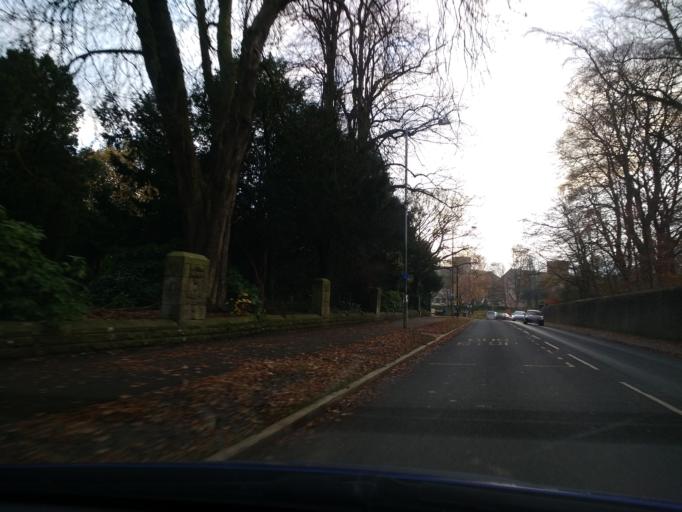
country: GB
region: England
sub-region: Lancashire
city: Lancaster
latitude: 54.0489
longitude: -2.7768
